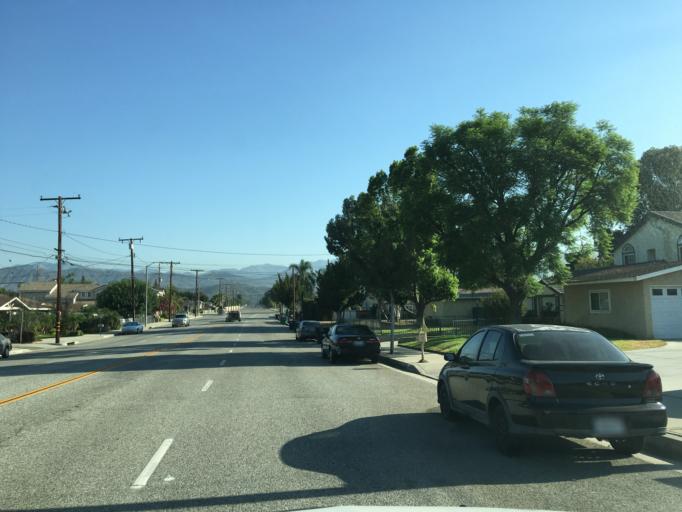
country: US
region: California
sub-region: Los Angeles County
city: Charter Oak
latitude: 34.0942
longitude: -117.8464
